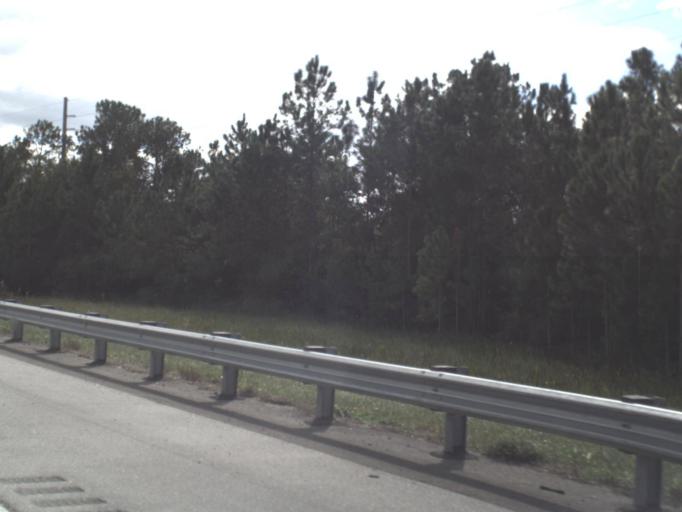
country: US
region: Florida
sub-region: Osceola County
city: Buenaventura Lakes
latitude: 28.3103
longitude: -81.3675
